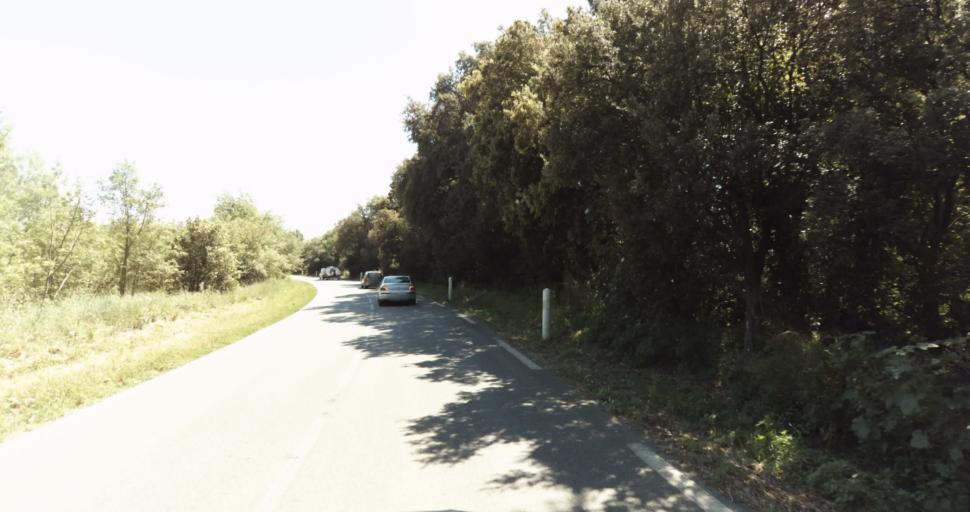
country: FR
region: Provence-Alpes-Cote d'Azur
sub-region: Departement du Var
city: Hyeres
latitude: 43.1352
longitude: 6.1578
